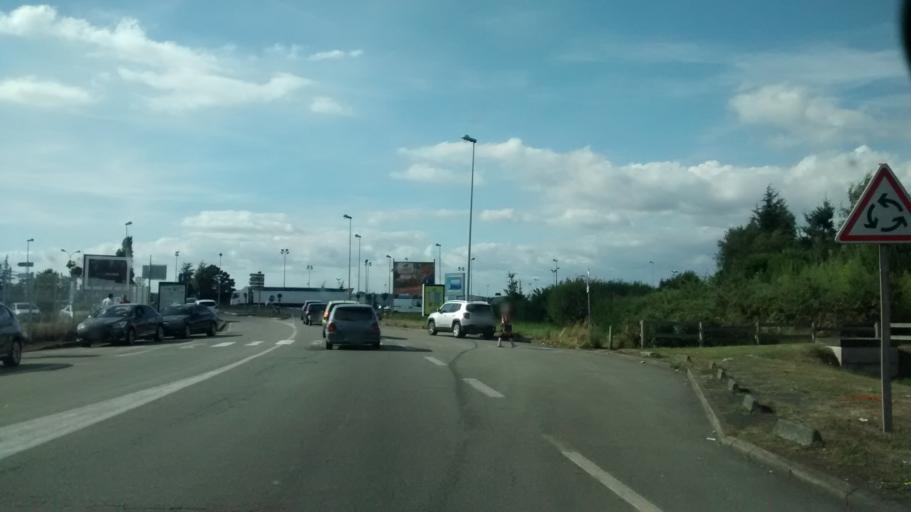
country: FR
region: Pays de la Loire
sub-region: Departement de la Loire-Atlantique
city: Bouguenais
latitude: 47.1582
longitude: -1.5974
